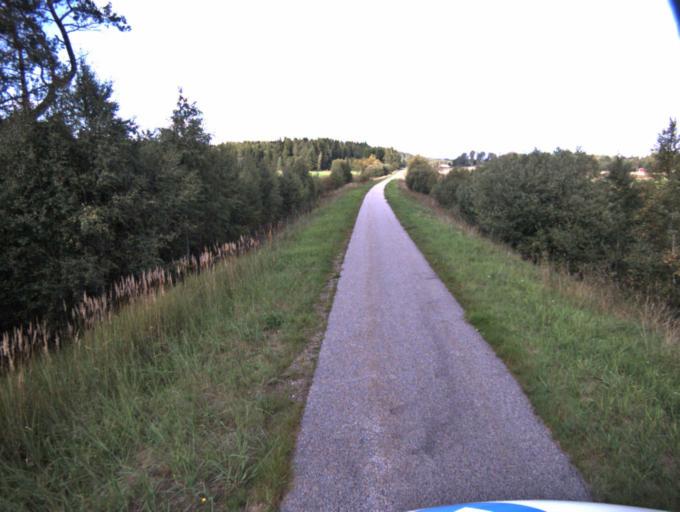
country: SE
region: Vaestra Goetaland
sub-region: Ulricehamns Kommun
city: Ulricehamn
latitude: 57.8758
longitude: 13.4281
